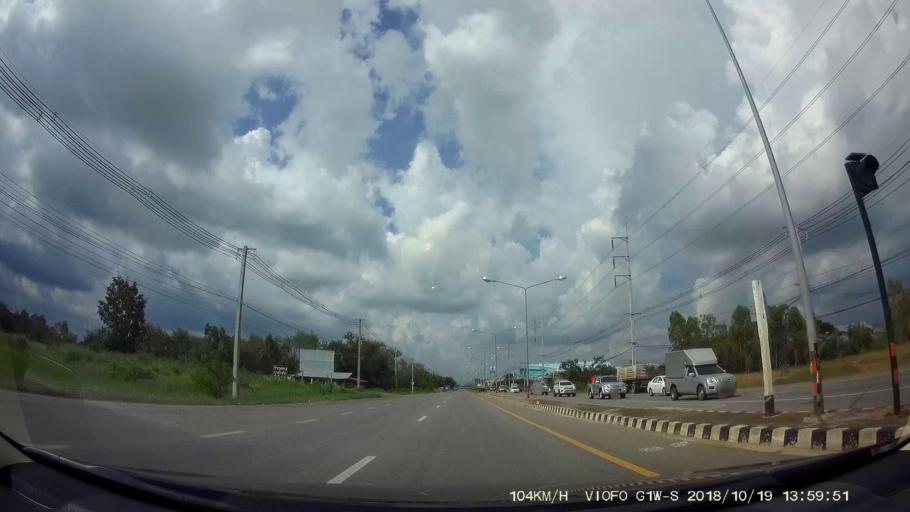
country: TH
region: Chaiyaphum
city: Chaiyaphum
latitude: 15.8159
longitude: 102.0602
